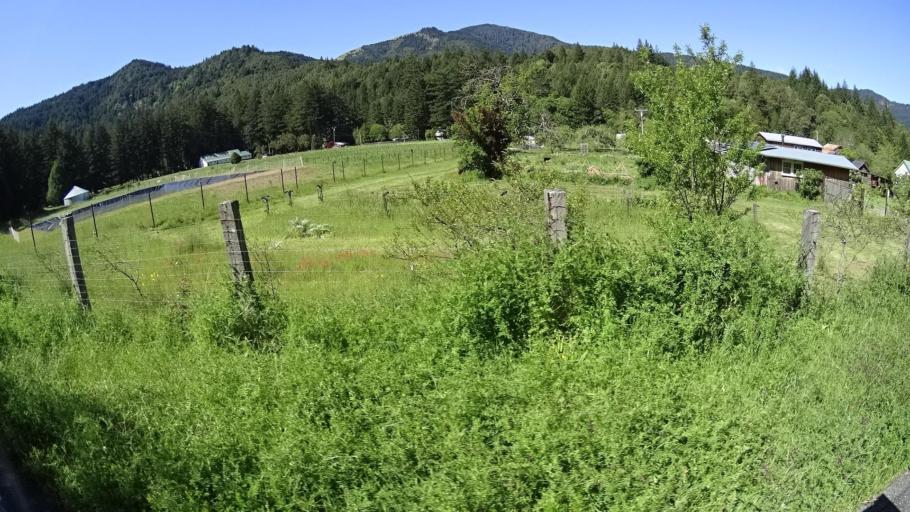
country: US
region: California
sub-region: Humboldt County
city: Rio Dell
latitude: 40.2730
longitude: -124.2305
